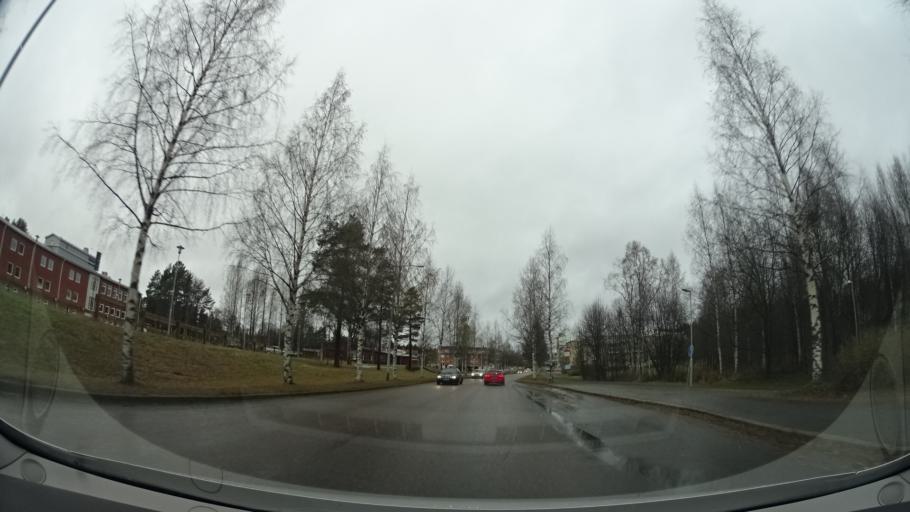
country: SE
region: Vaesterbotten
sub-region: Skelleftea Kommun
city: Skelleftea
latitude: 64.7587
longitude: 20.9581
